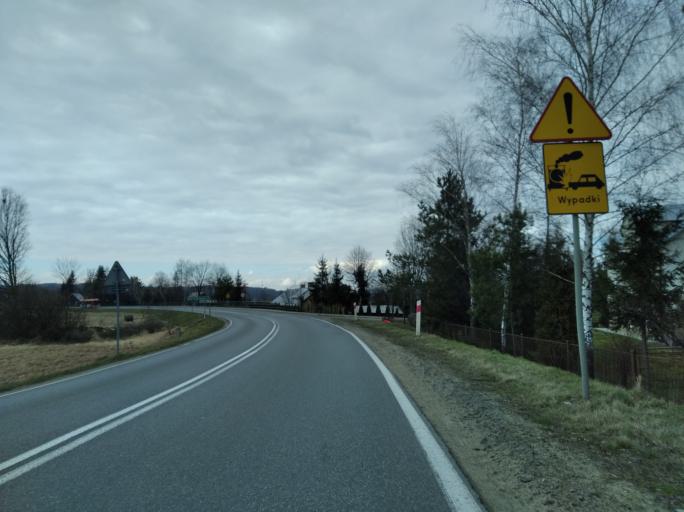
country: PL
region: Subcarpathian Voivodeship
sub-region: Powiat krosnienski
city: Wojaszowka
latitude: 49.7916
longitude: 21.6590
